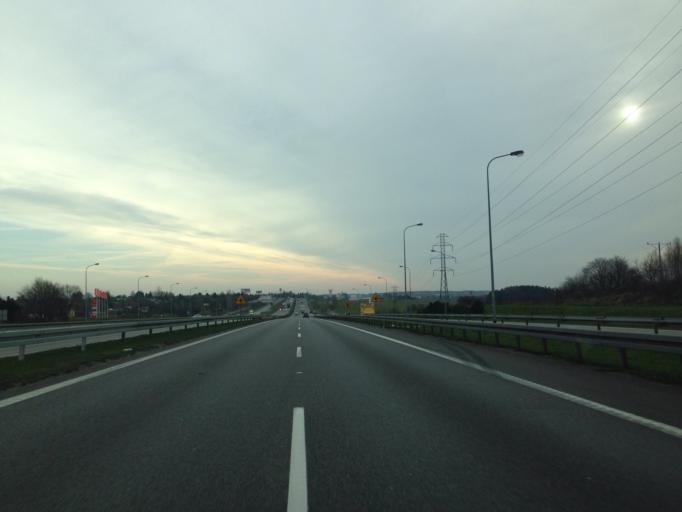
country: PL
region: Pomeranian Voivodeship
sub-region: Powiat gdanski
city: Kowale
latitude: 54.3741
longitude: 18.5148
